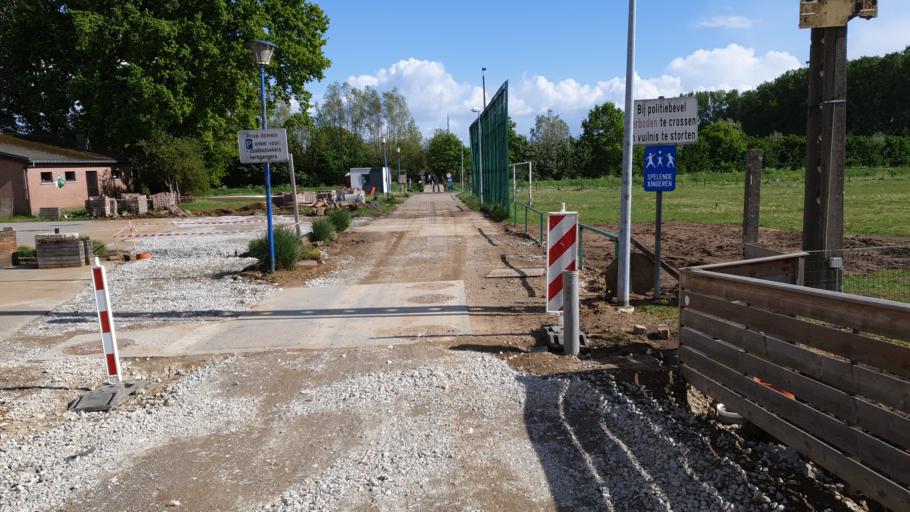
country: BE
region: Flanders
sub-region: Provincie Vlaams-Brabant
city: Aarschot
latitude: 50.9931
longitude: 4.8691
